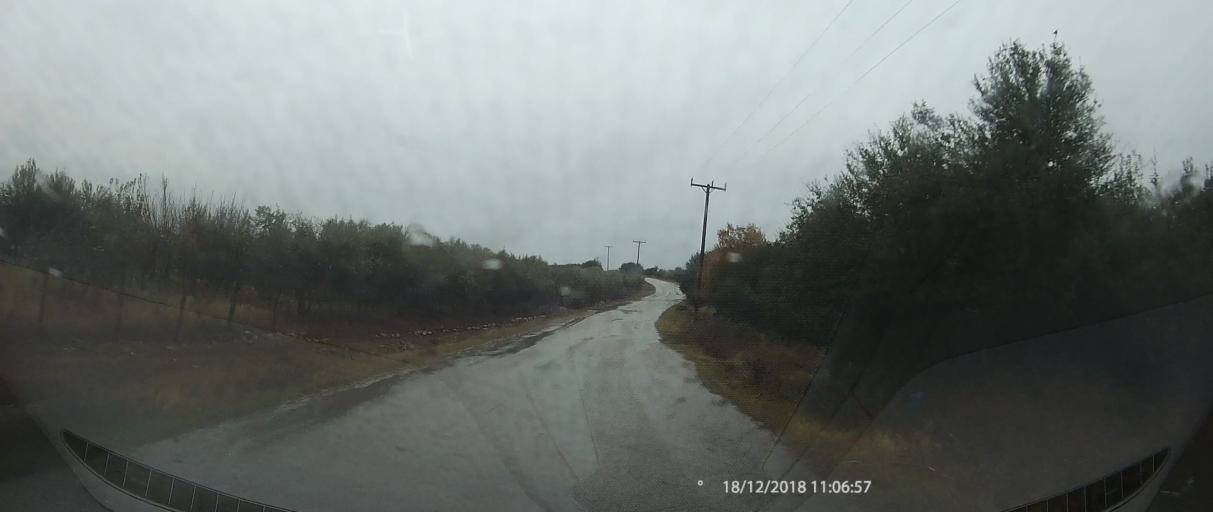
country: GR
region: Central Macedonia
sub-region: Nomos Pierias
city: Kato Milia
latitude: 40.2231
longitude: 22.3295
